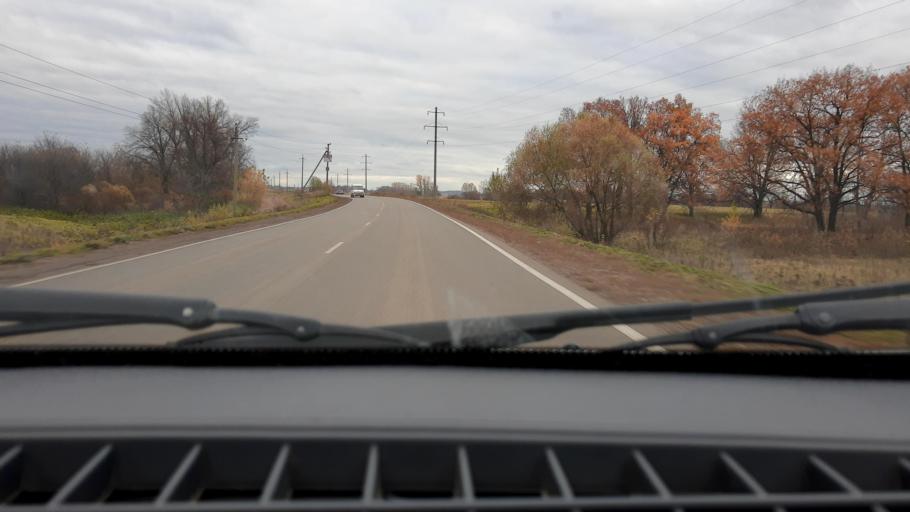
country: RU
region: Bashkortostan
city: Kabakovo
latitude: 54.5652
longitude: 55.9912
